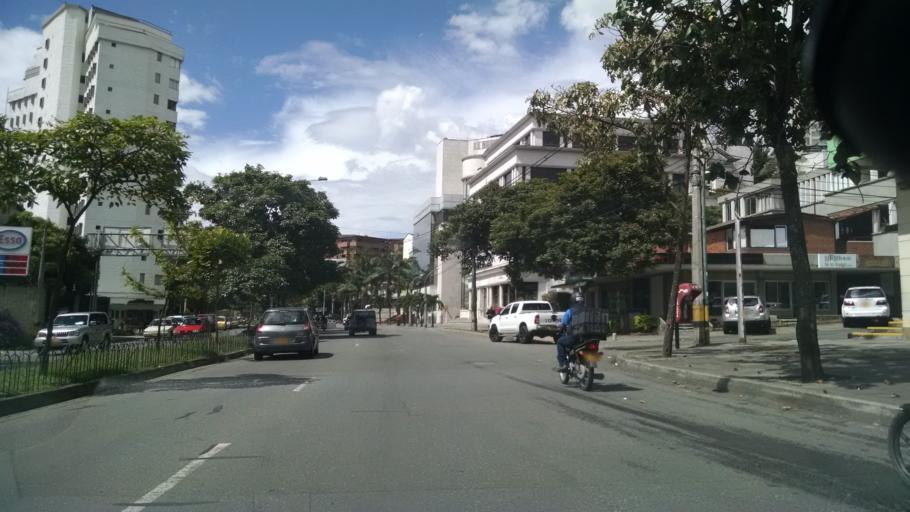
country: CO
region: Antioquia
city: Itagui
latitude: 6.2114
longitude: -75.5701
